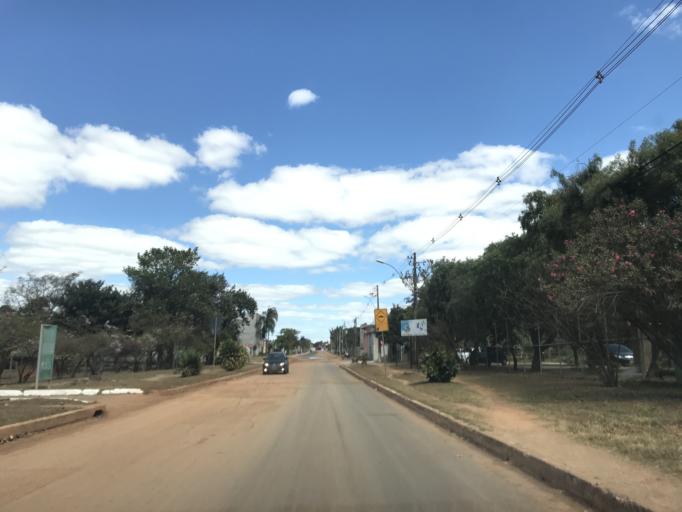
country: BR
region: Federal District
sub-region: Brasilia
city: Brasilia
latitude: -15.7921
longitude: -48.0229
